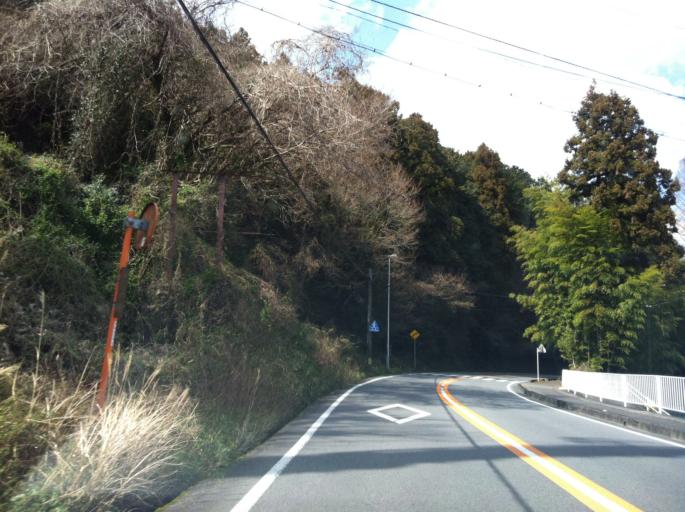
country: JP
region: Shizuoka
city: Kanaya
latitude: 34.8165
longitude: 138.1330
